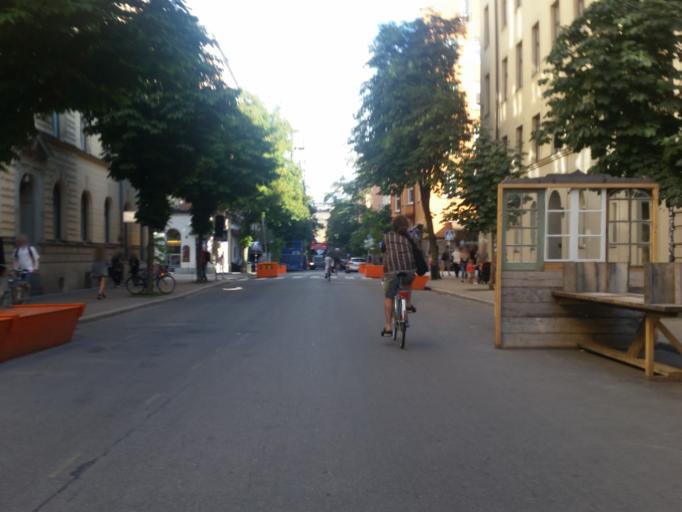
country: SE
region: Stockholm
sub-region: Stockholms Kommun
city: Stockholm
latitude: 59.3157
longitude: 18.0641
